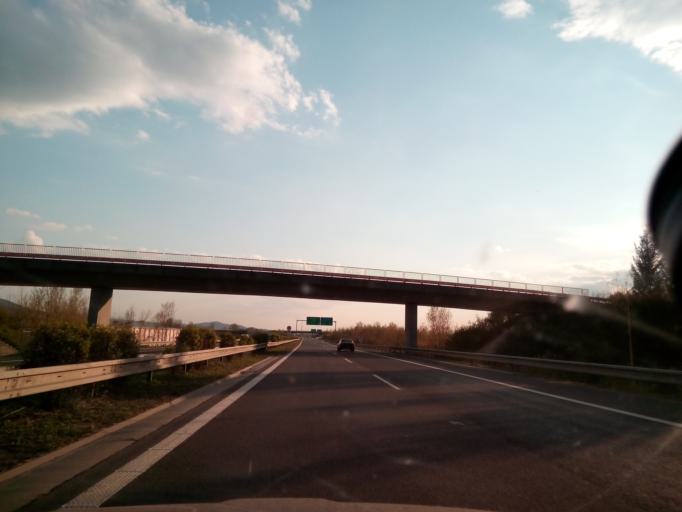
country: SK
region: Nitriansky
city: Ilava
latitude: 49.0053
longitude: 18.2285
